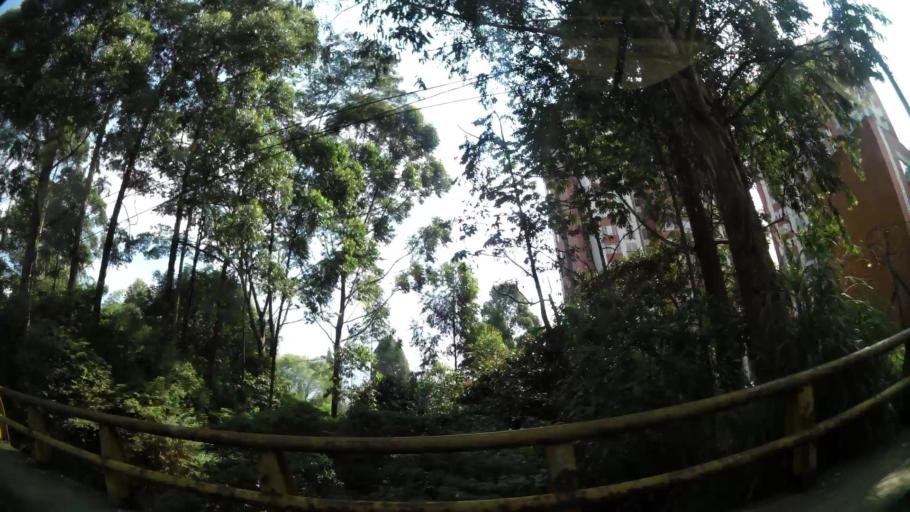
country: CO
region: Antioquia
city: La Estrella
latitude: 6.1682
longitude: -75.6494
